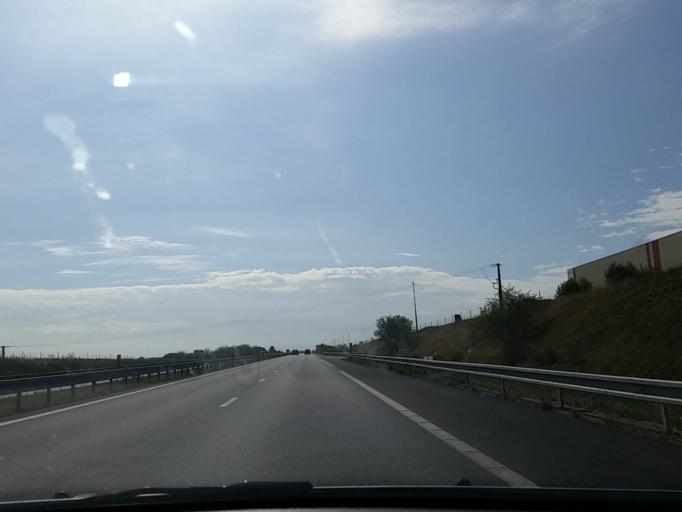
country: FR
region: Centre
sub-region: Departement du Cher
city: La Chapelle-Saint-Ursin
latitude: 47.0533
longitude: 2.3164
